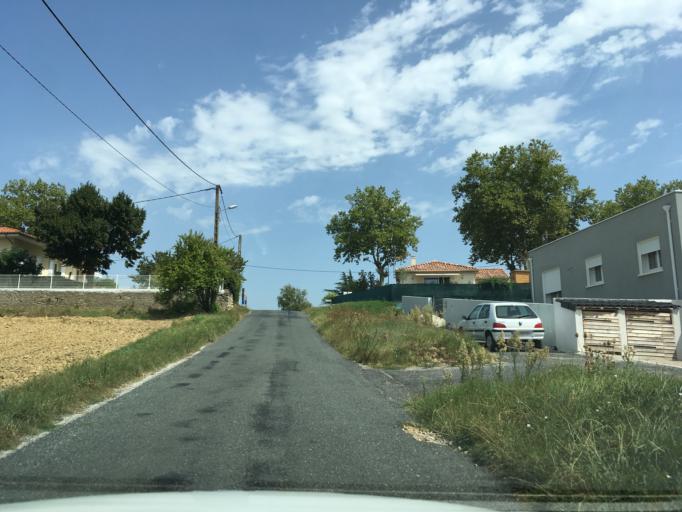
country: FR
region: Midi-Pyrenees
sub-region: Departement du Tarn
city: Castres
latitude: 43.6158
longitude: 2.2289
